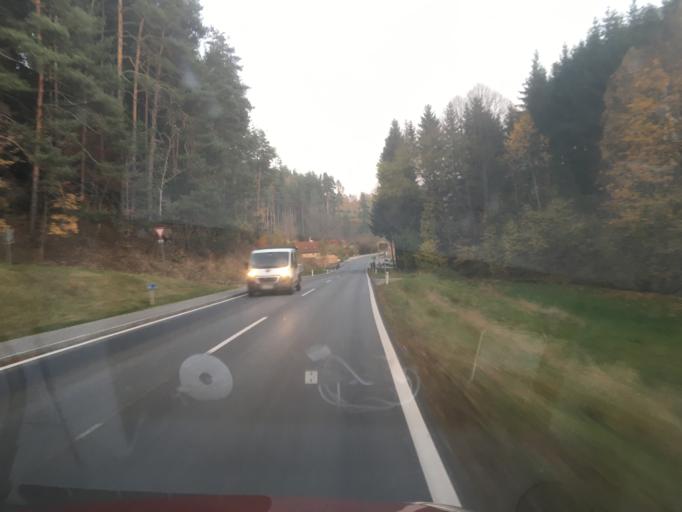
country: AT
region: Lower Austria
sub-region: Politischer Bezirk Zwettl
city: Gross-Gerungs
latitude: 48.5723
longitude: 14.9685
